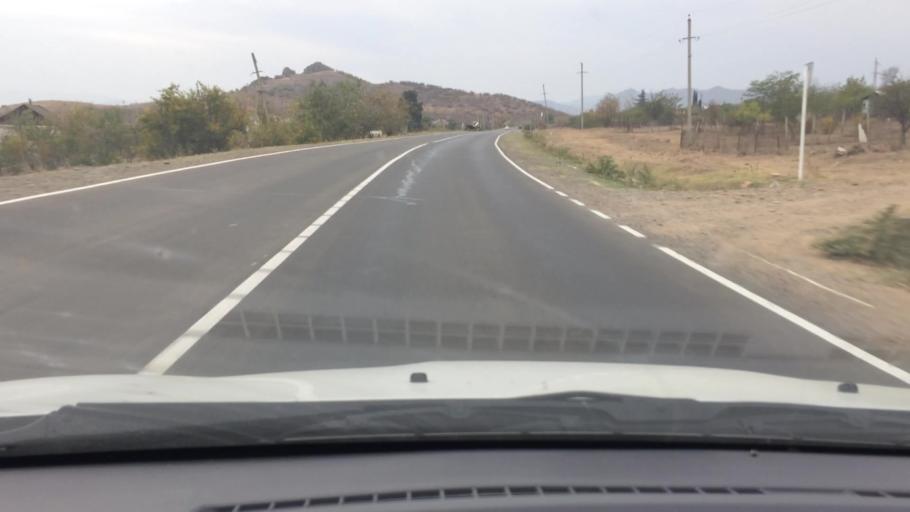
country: GE
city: Naghvarevi
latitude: 41.3568
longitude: 44.8304
